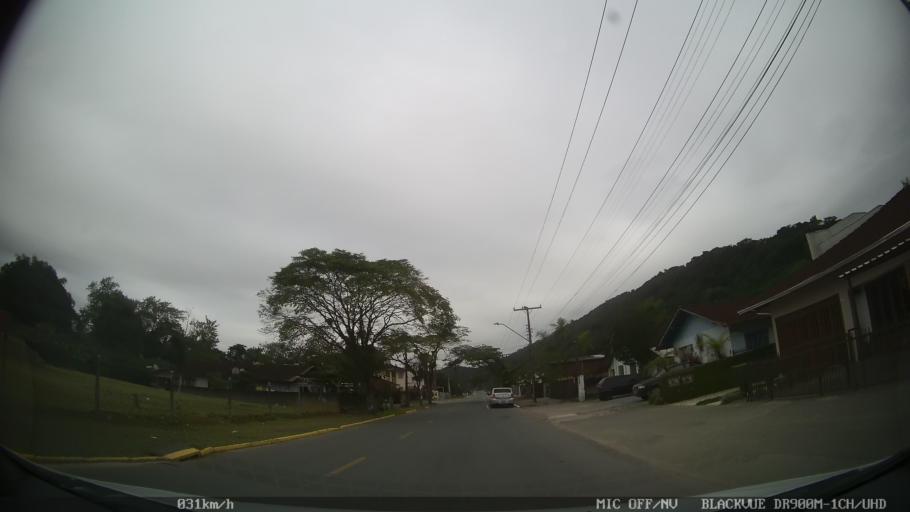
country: BR
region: Santa Catarina
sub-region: Joinville
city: Joinville
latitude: -26.2050
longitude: -48.9130
